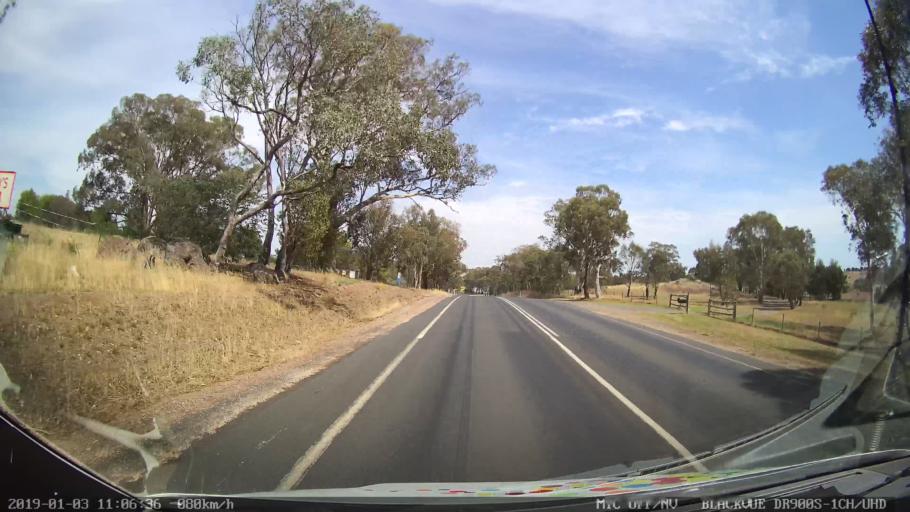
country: AU
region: New South Wales
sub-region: Young
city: Young
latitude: -34.2642
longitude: 148.2713
